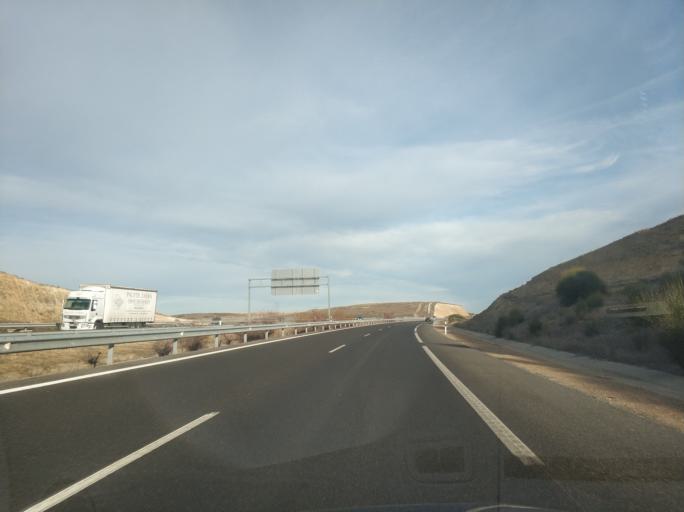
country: ES
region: Castille and Leon
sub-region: Provincia de Salamanca
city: Villamayor
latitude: 41.0058
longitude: -5.6790
